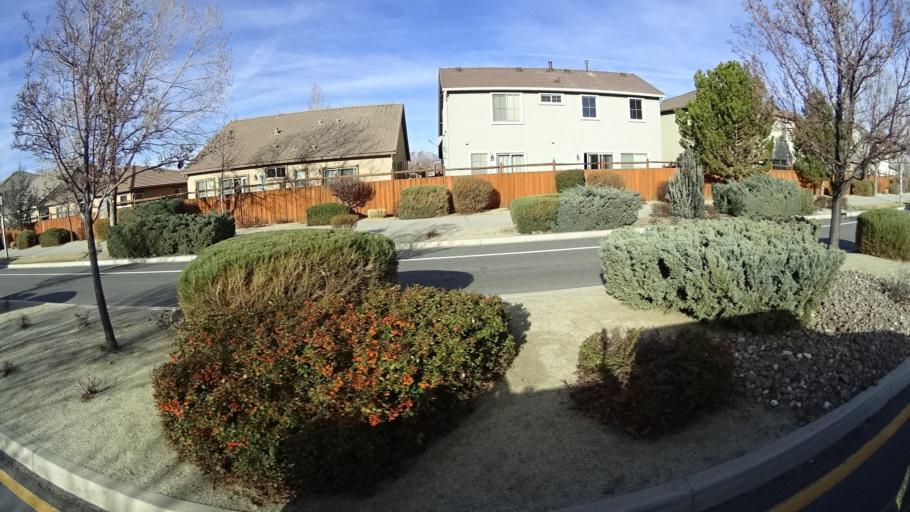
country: US
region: Nevada
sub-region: Washoe County
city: Spanish Springs
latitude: 39.6214
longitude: -119.6698
